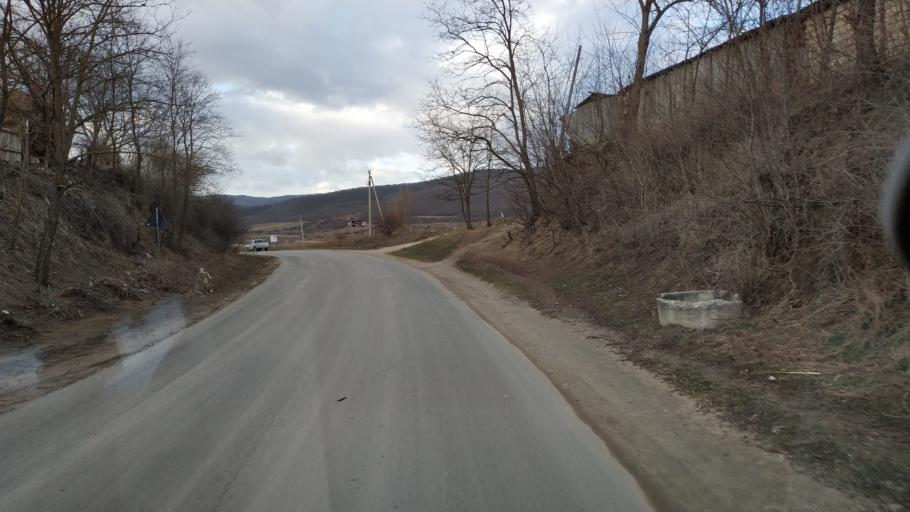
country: MD
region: Calarasi
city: Calarasi
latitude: 47.3072
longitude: 28.3608
